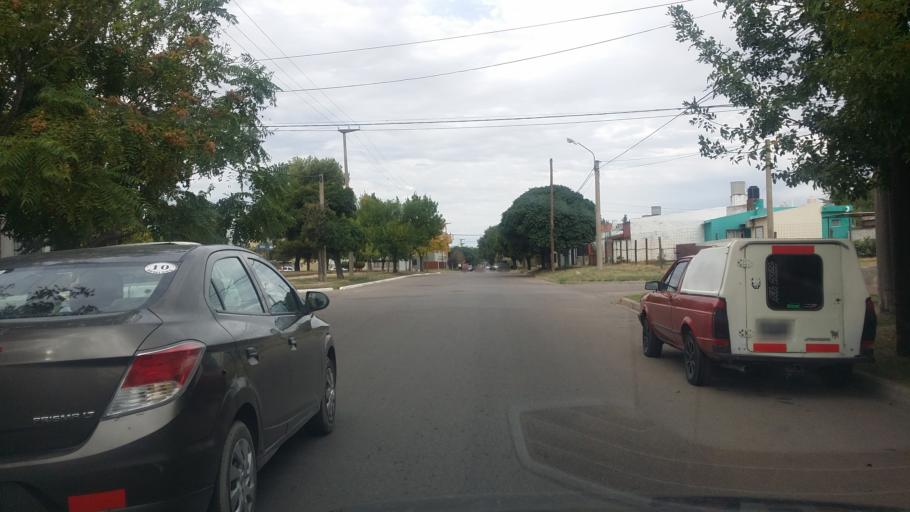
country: AR
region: La Pampa
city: Santa Rosa
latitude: -36.6367
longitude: -64.2890
